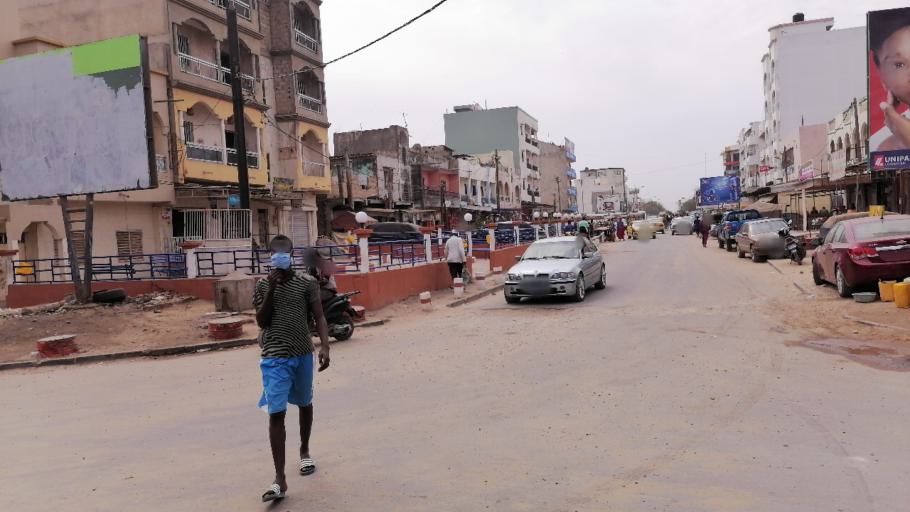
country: SN
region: Dakar
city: Pikine
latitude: 14.7656
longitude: -17.3898
